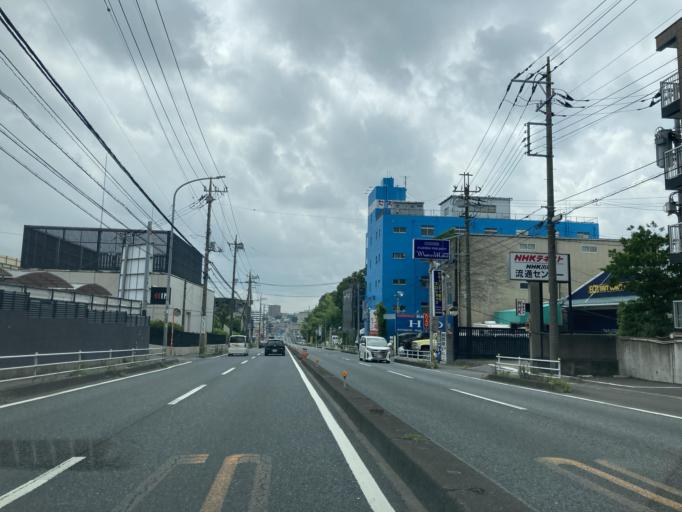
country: JP
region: Saitama
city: Asaka
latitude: 35.7950
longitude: 139.5733
